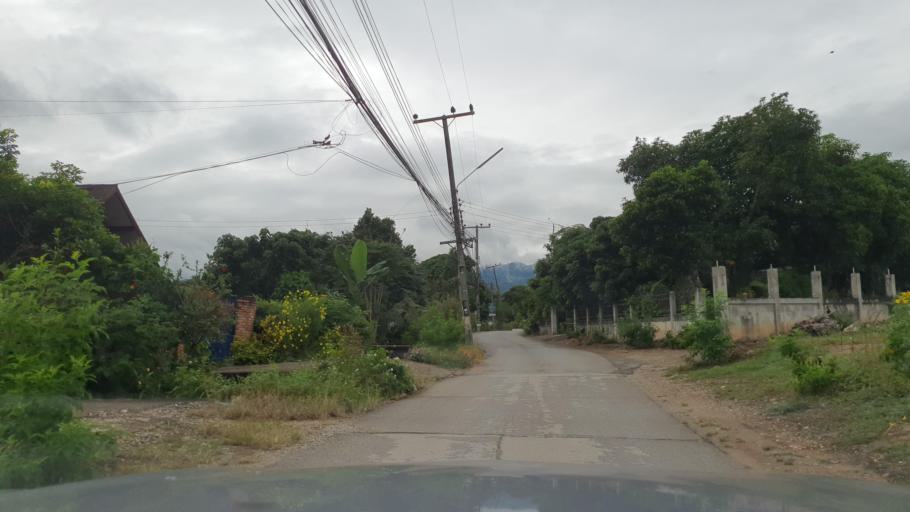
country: TH
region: Chiang Mai
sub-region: Amphoe Chiang Dao
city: Chiang Dao
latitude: 19.3295
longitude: 98.9529
